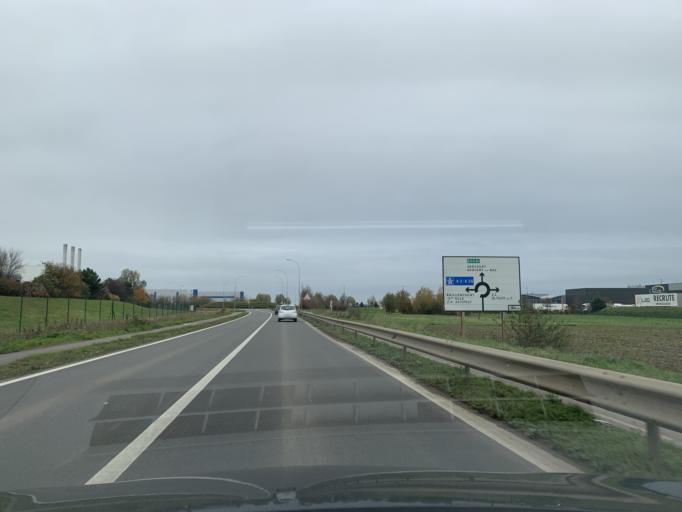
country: FR
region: Nord-Pas-de-Calais
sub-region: Departement du Nord
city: Neuville-Saint-Remy
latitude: 50.1996
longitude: 3.2023
